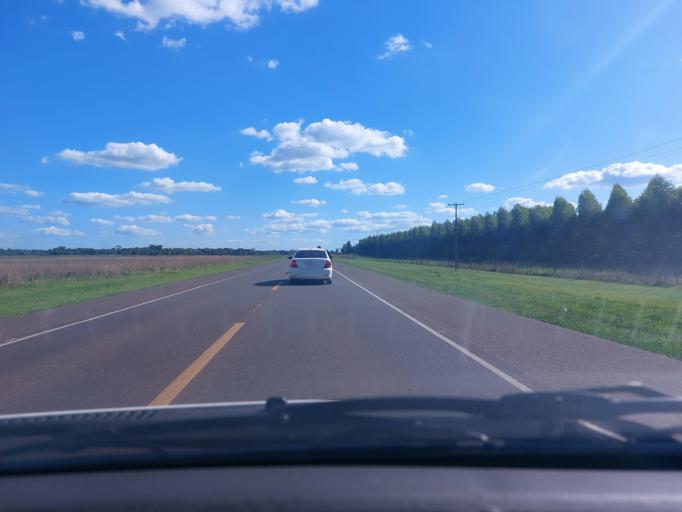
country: PY
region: San Pedro
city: Union
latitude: -24.6935
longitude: -56.4880
